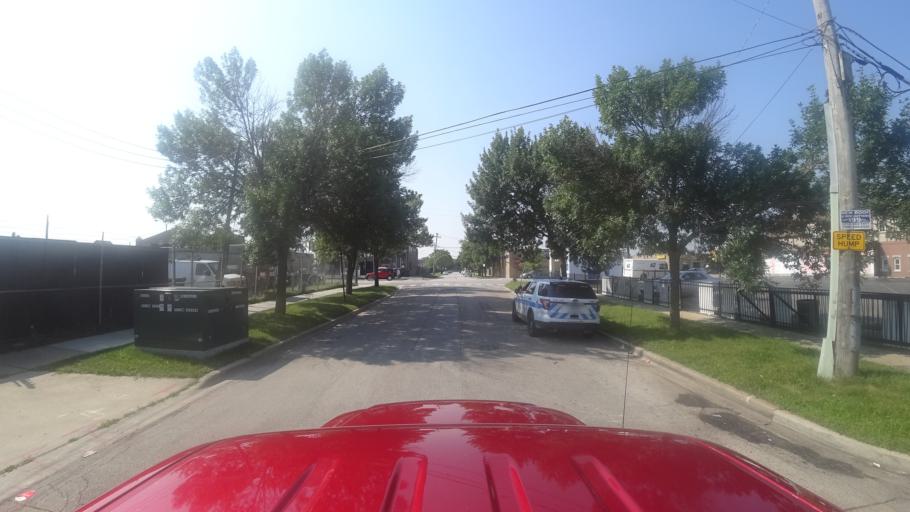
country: US
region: Illinois
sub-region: Cook County
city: Cicero
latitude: 41.7998
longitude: -87.7393
